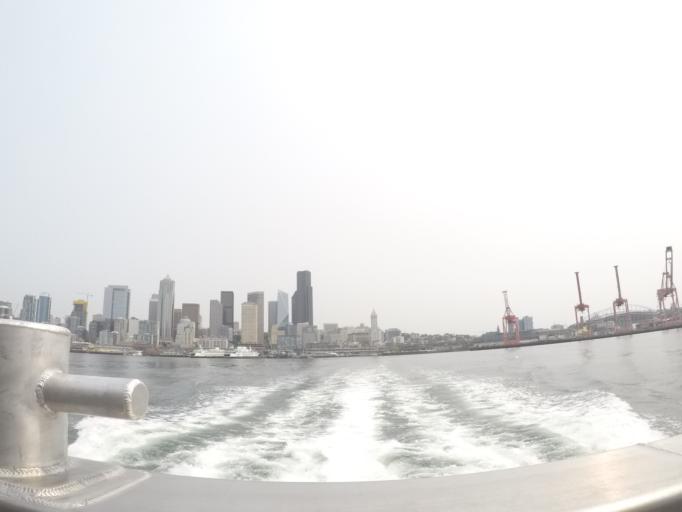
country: US
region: Washington
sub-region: King County
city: Seattle
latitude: 47.5989
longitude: -122.3485
